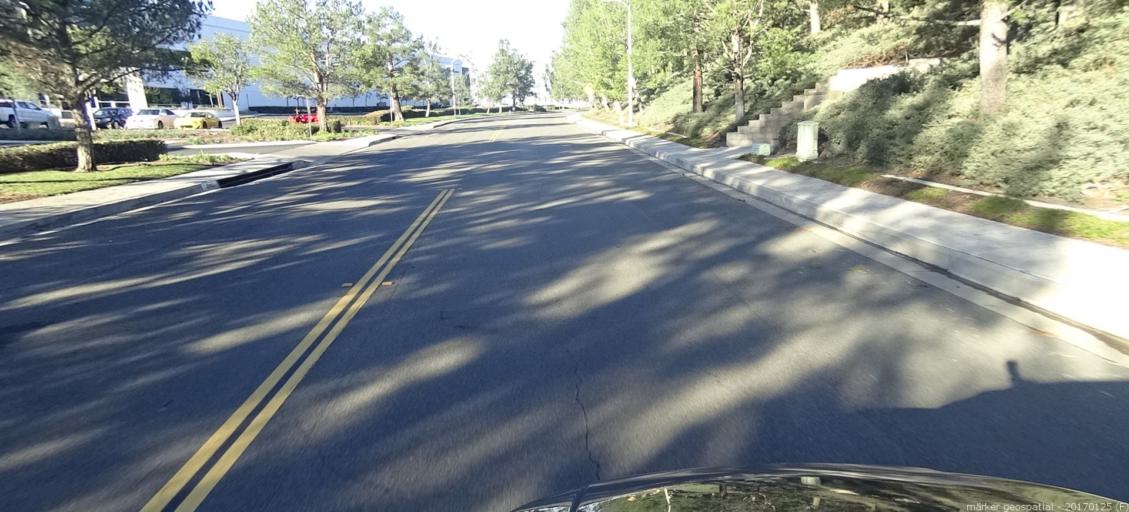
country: US
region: California
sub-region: Orange County
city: Foothill Ranch
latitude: 33.6785
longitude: -117.6522
